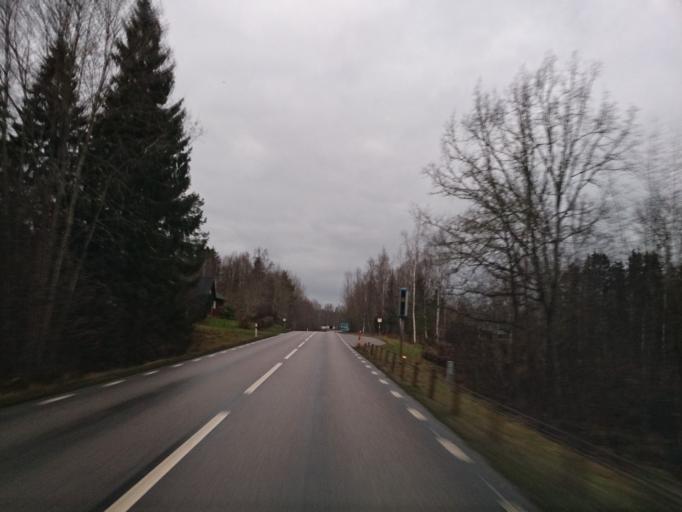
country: SE
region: OEstergoetland
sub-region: Atvidabergs Kommun
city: Atvidaberg
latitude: 58.2474
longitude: 15.9319
